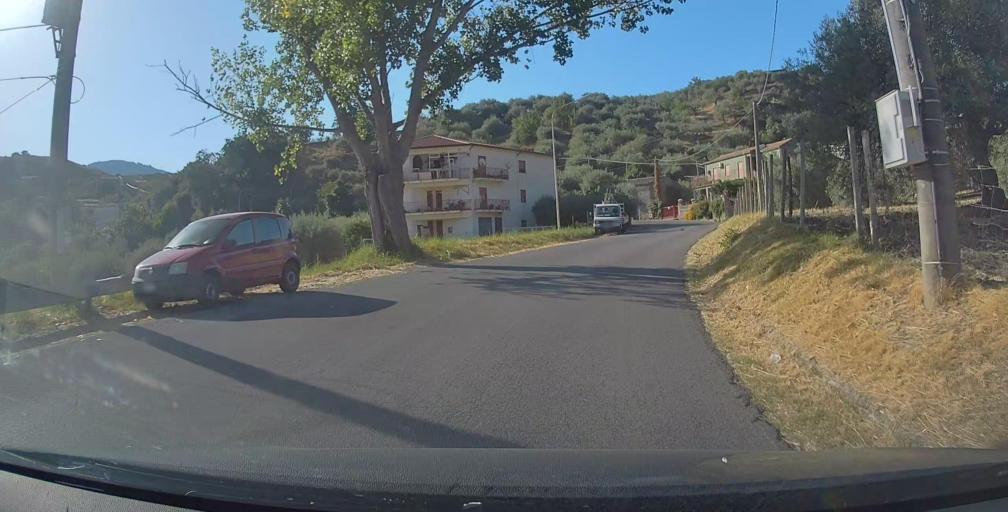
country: IT
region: Sicily
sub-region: Messina
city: San Piero Patti
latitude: 38.0770
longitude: 14.9764
